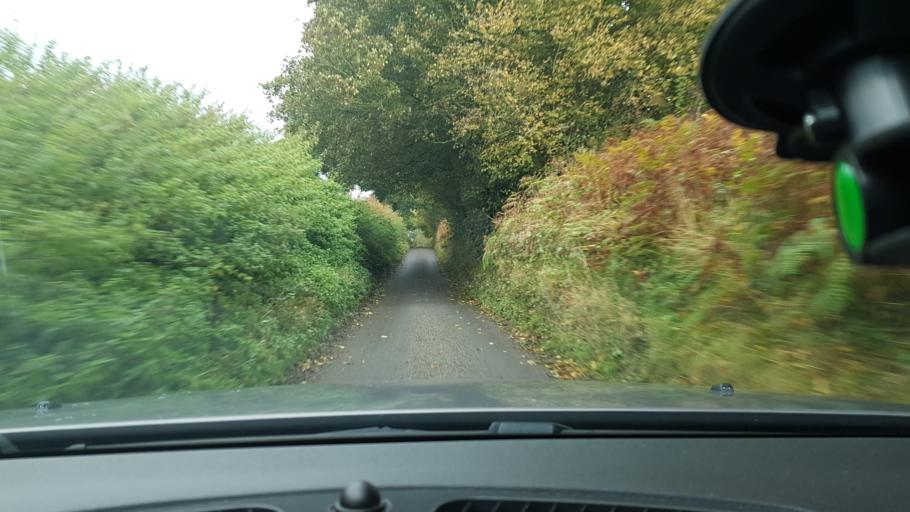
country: GB
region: England
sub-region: Wiltshire
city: Burbage
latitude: 51.3558
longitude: -1.7036
